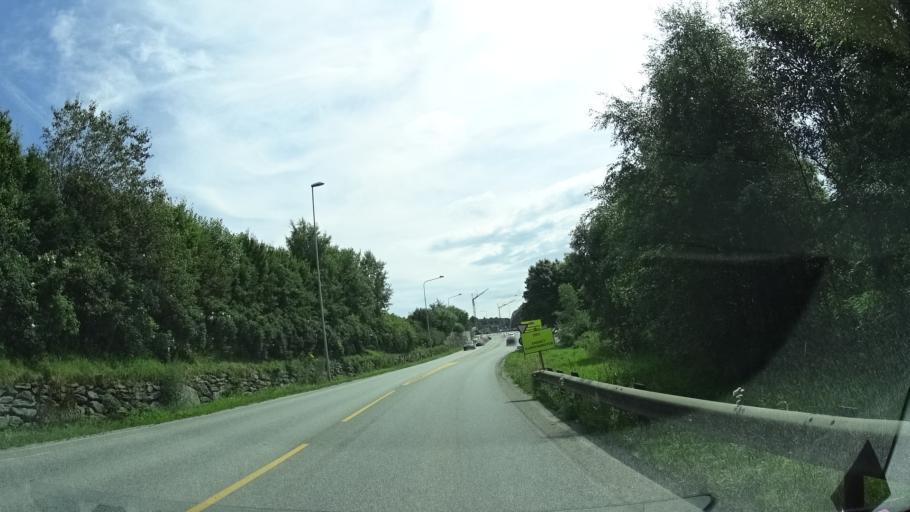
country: NO
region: Rogaland
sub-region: Stavanger
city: Stavanger
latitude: 58.9816
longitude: 5.6816
